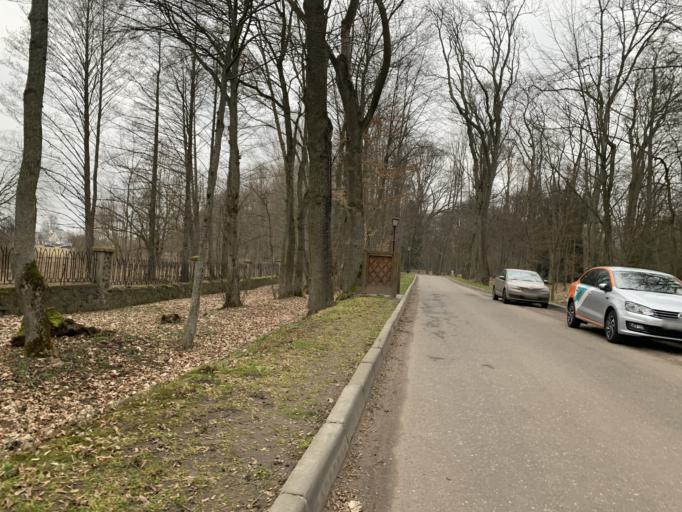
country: BY
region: Minsk
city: Nyasvizh
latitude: 53.2250
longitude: 26.6915
